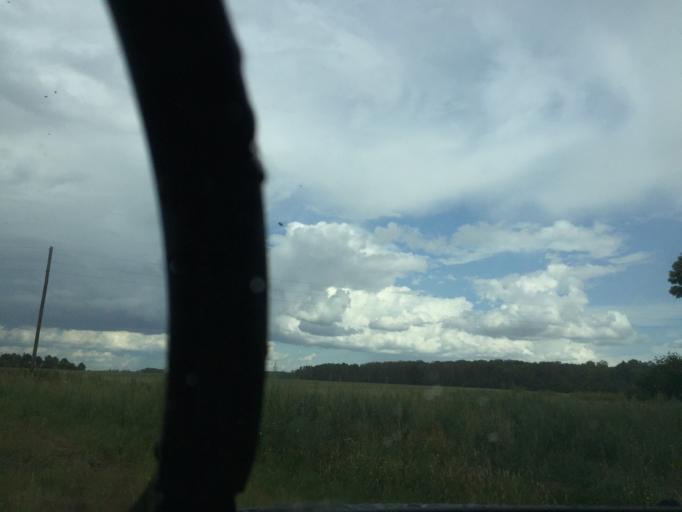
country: LT
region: Siauliu apskritis
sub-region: Joniskis
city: Joniskis
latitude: 56.3431
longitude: 23.5519
